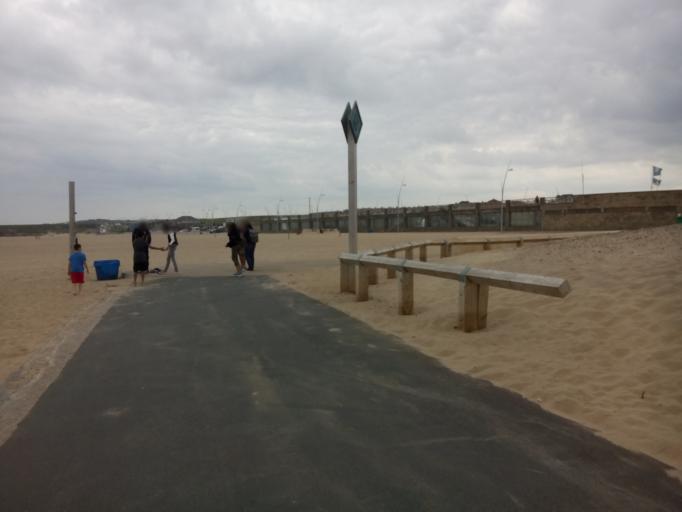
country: GB
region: England
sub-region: South Tyneside
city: South Shields
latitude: 54.9988
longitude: -1.4116
